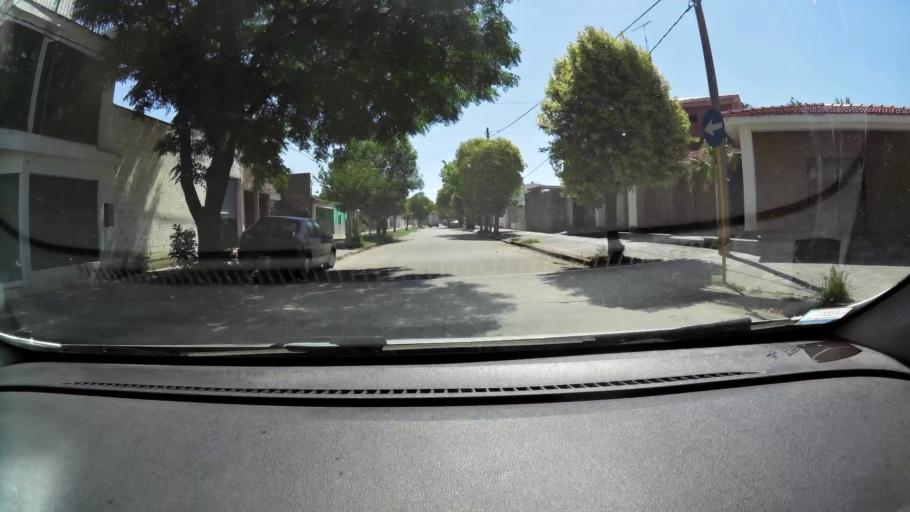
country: AR
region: Cordoba
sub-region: Departamento de Capital
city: Cordoba
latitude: -31.3777
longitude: -64.1417
